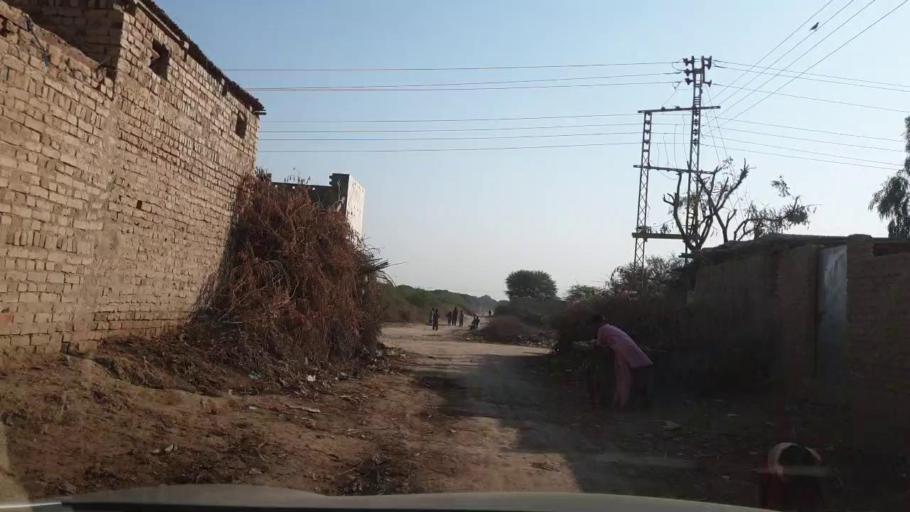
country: PK
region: Sindh
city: Tando Allahyar
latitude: 25.5035
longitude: 68.8501
